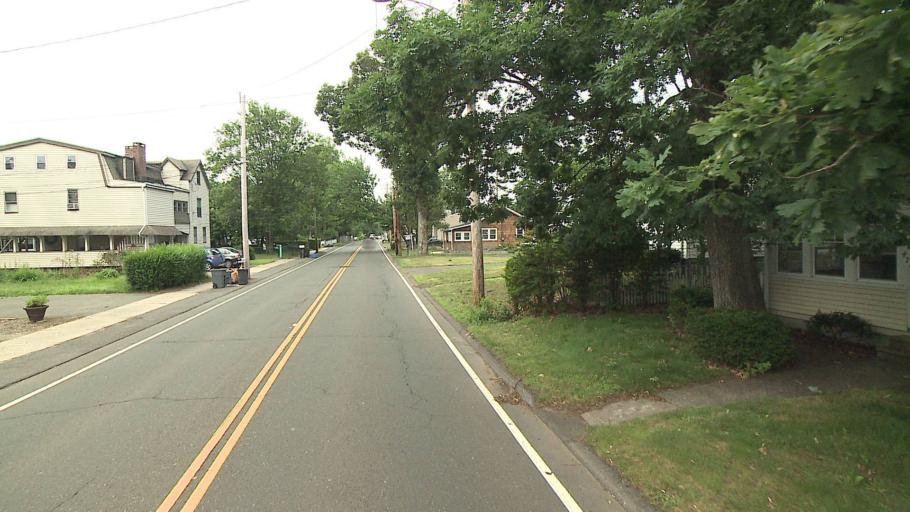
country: US
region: Connecticut
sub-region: New Haven County
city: Woodmont
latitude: 41.2382
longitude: -72.9728
